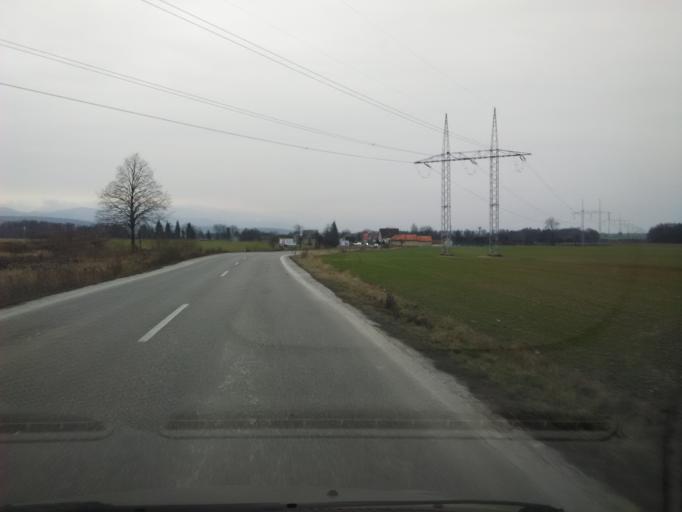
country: SK
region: Nitriansky
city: Prievidza
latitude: 48.8317
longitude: 18.6437
